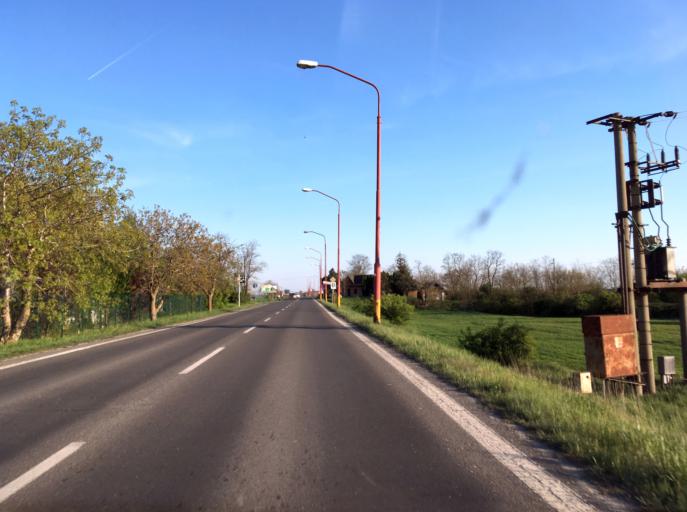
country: HU
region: Gyor-Moson-Sopron
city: Rajka
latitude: 48.0347
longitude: 17.1643
